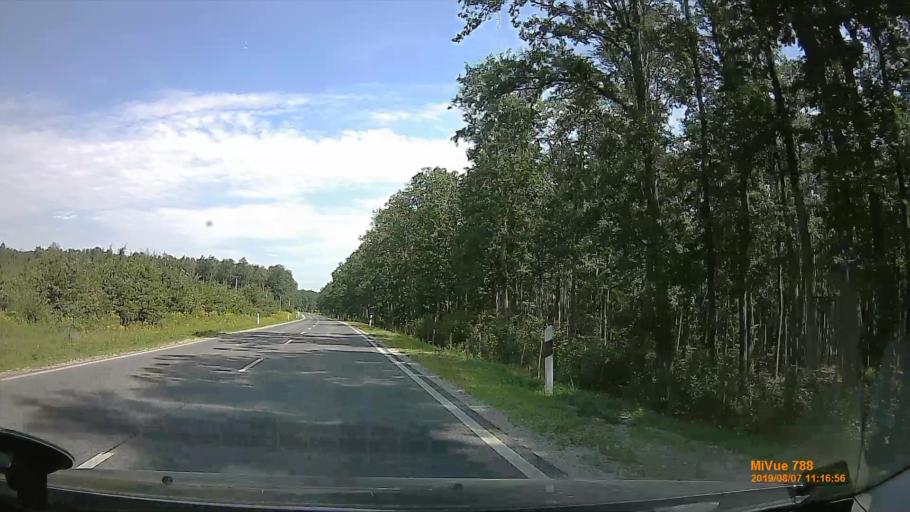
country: HU
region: Zala
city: Lenti
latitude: 46.7337
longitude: 16.5527
